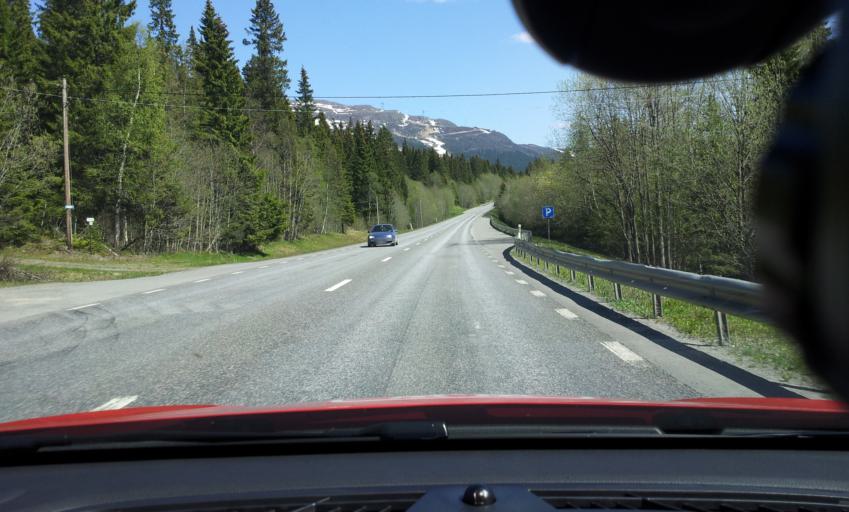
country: SE
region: Jaemtland
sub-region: Are Kommun
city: Are
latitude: 63.4018
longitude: 12.9872
